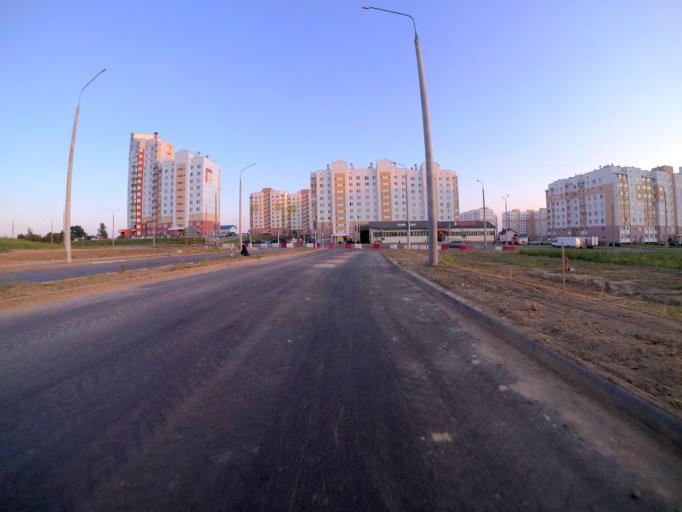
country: BY
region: Grodnenskaya
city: Hrodna
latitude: 53.7140
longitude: 23.8675
